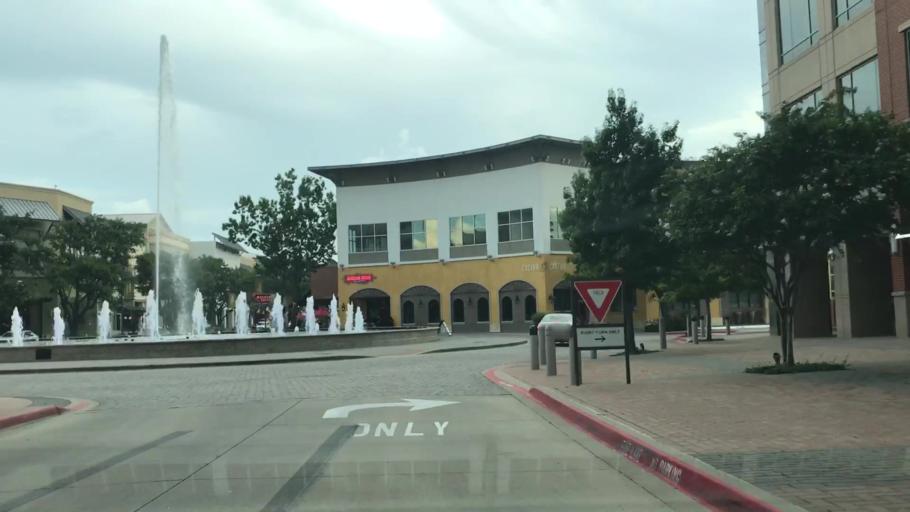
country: US
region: Texas
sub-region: Denton County
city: The Colony
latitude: 33.0810
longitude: -96.8232
